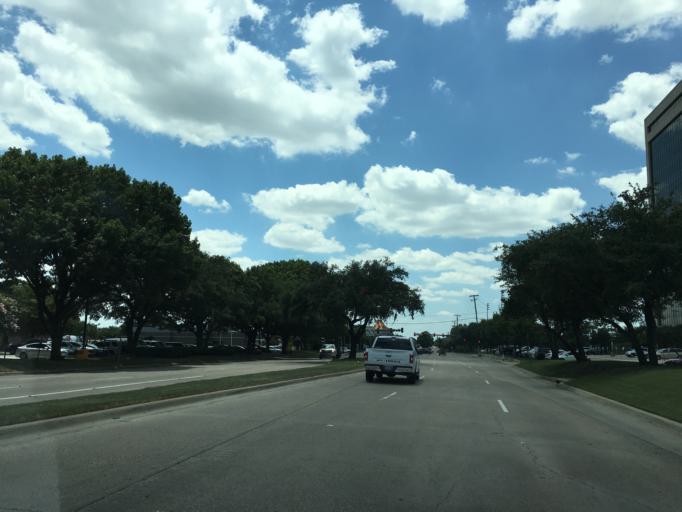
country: US
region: Texas
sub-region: Dallas County
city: Addison
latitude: 32.9400
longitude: -96.8368
